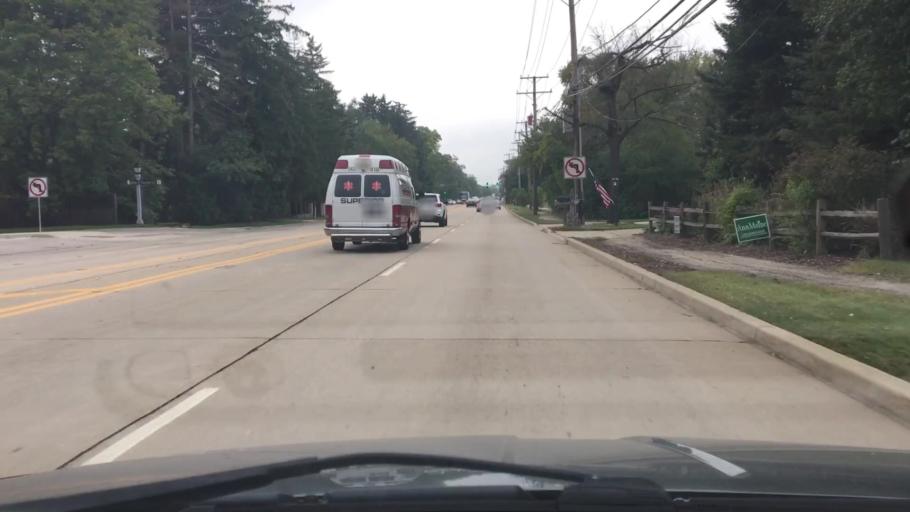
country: US
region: Illinois
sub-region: Lake County
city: Lincolnshire
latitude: 42.2005
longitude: -87.9123
